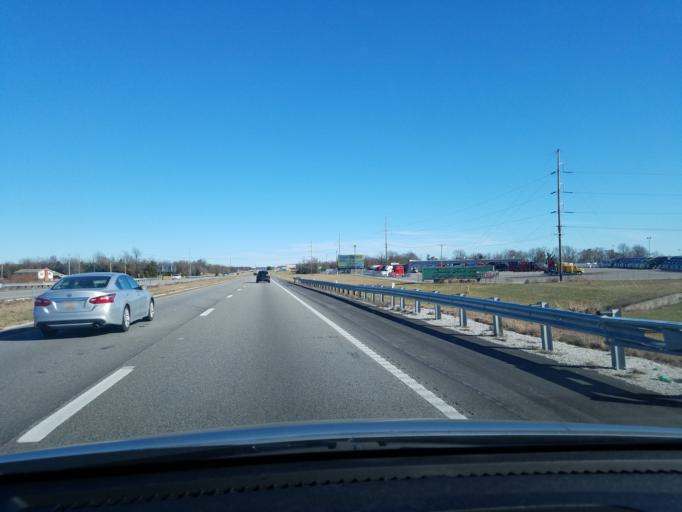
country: US
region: Missouri
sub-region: Greene County
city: Strafford
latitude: 37.2539
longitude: -93.1720
